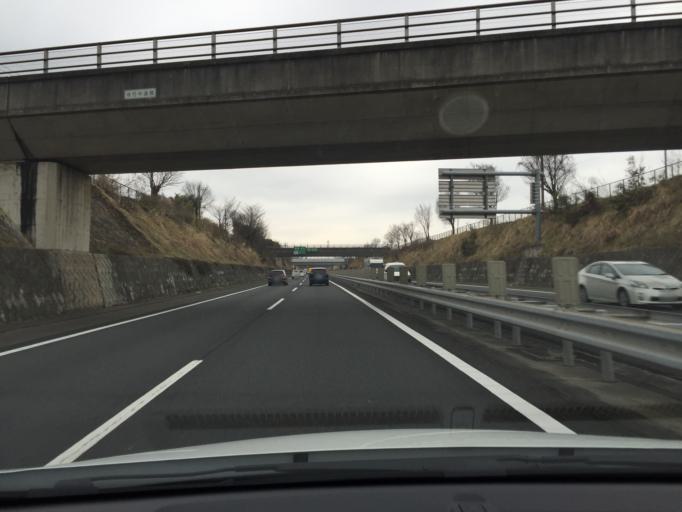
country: JP
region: Saitama
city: Hanno
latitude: 35.8041
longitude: 139.3359
